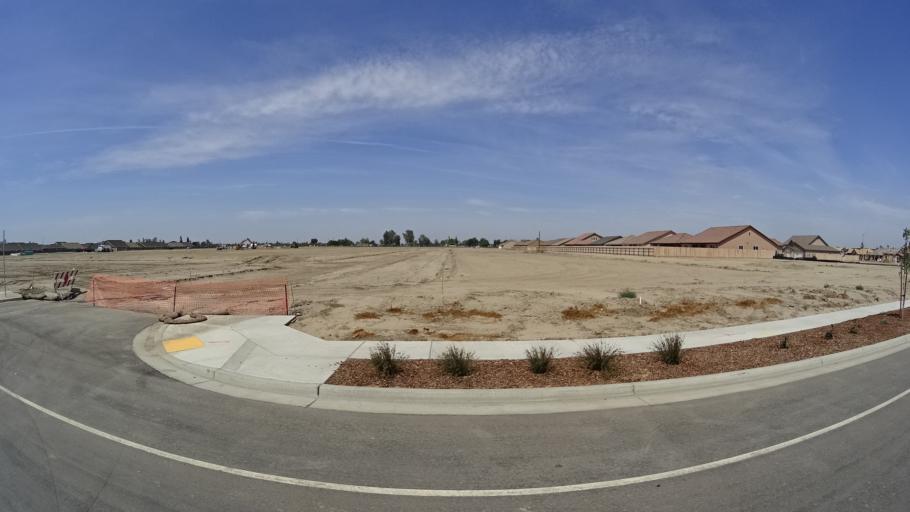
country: US
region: California
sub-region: Kings County
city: Lucerne
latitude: 36.3510
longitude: -119.6819
